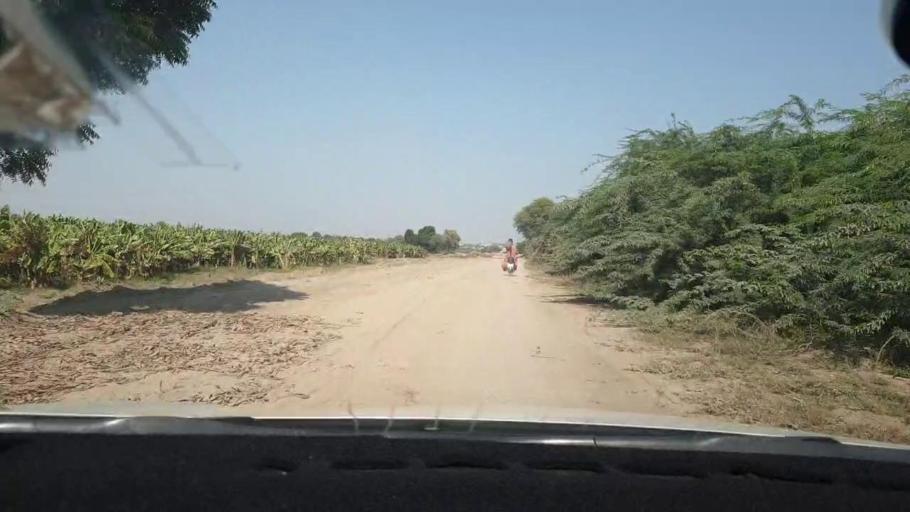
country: PK
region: Sindh
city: Tando Mittha Khan
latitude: 25.8667
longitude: 69.3852
